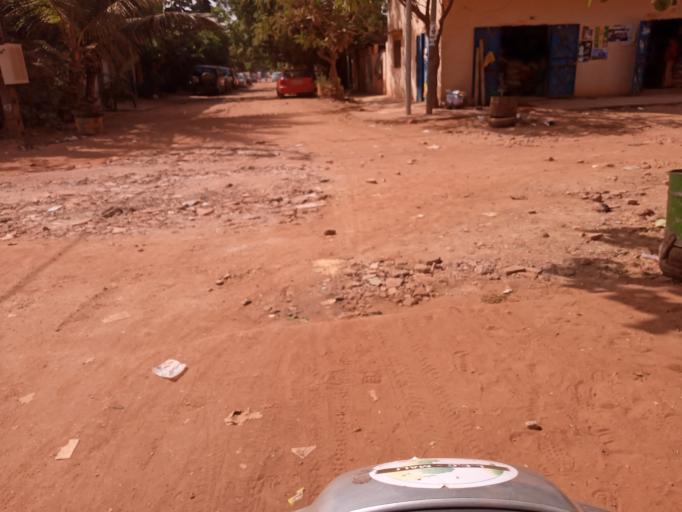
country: ML
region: Bamako
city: Bamako
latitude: 12.5856
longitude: -7.9497
